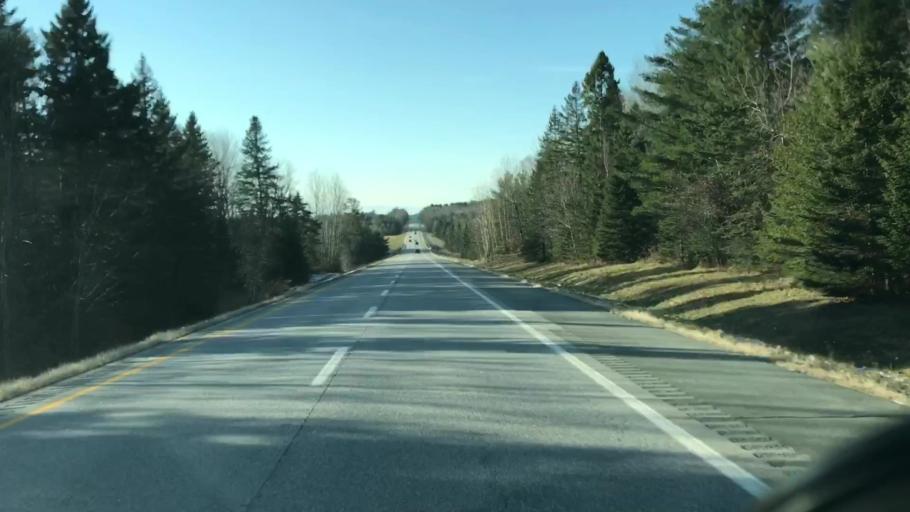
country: US
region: Maine
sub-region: Penobscot County
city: Carmel
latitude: 44.7752
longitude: -69.0376
